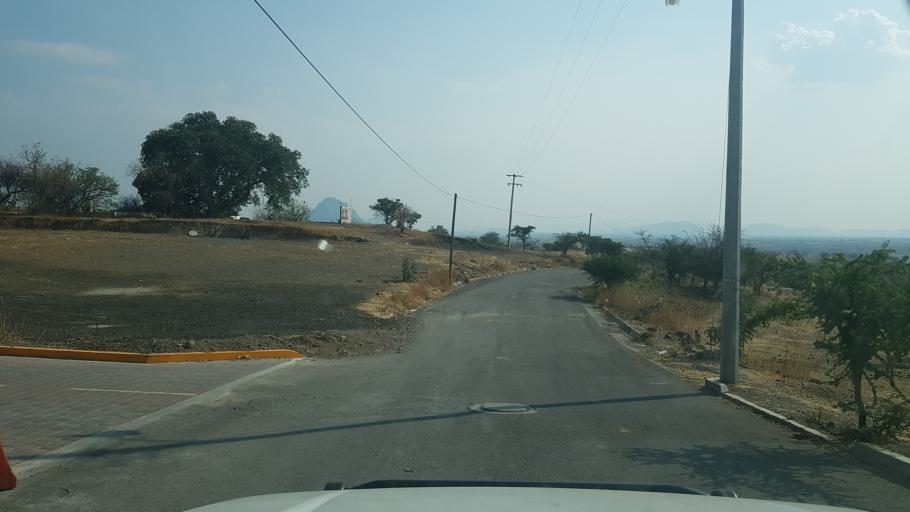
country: MX
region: Morelos
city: Tlacotepec
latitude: 18.7805
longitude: -98.7235
